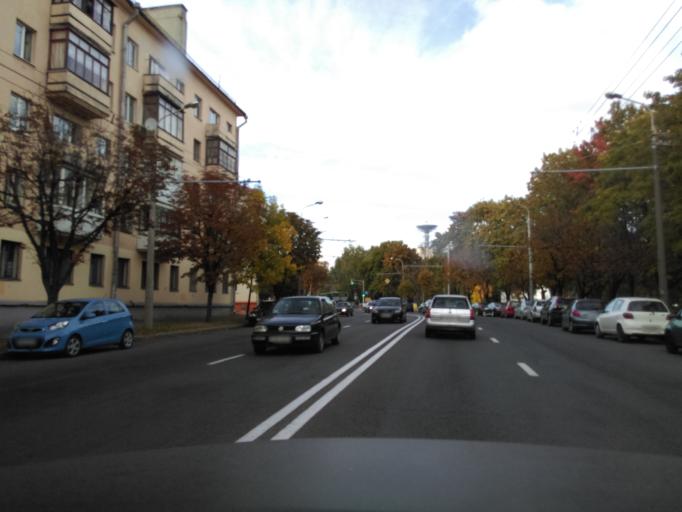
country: BY
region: Minsk
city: Minsk
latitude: 53.9178
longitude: 27.6036
